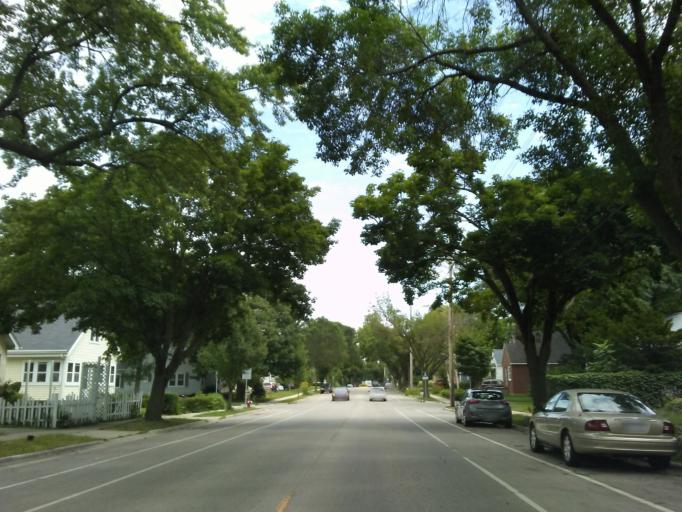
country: US
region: Wisconsin
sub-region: Dane County
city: Maple Bluff
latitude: 43.1068
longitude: -89.3498
